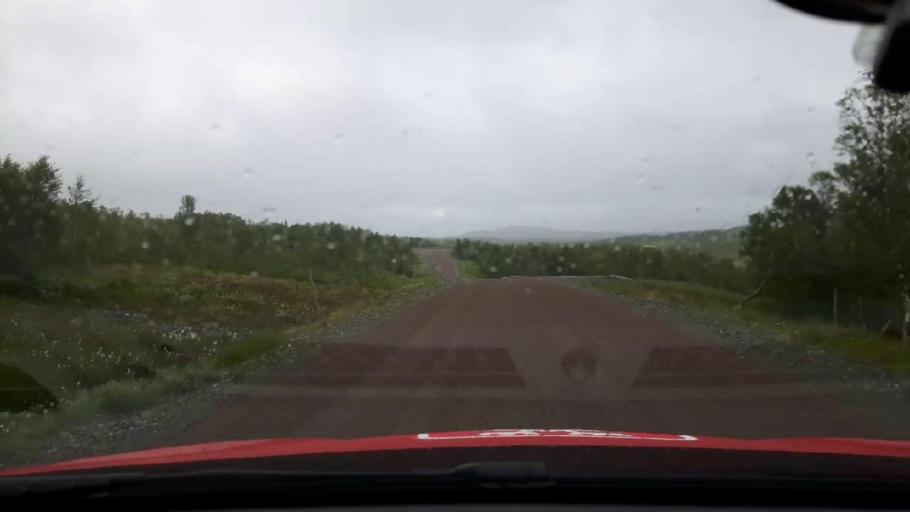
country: NO
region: Nord-Trondelag
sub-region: Meraker
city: Meraker
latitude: 63.1908
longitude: 12.3854
